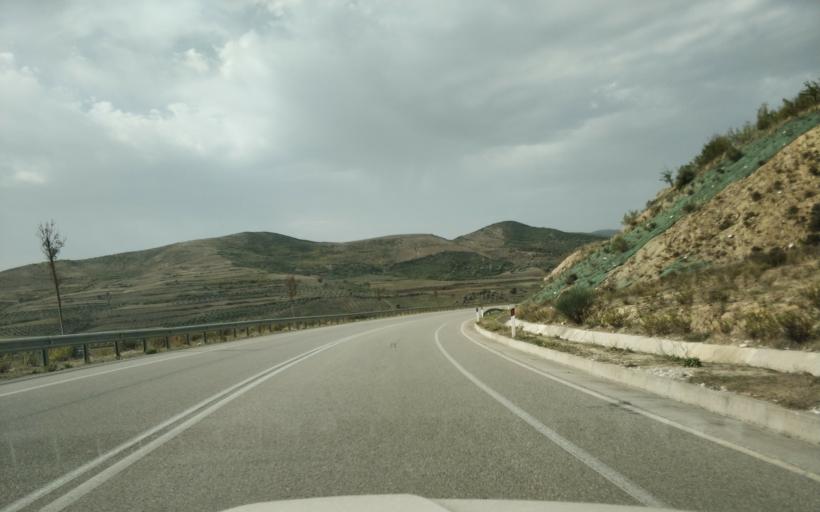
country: AL
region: Gjirokaster
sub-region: Rrethi i Tepelenes
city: Krahes
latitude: 40.3987
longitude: 19.8653
